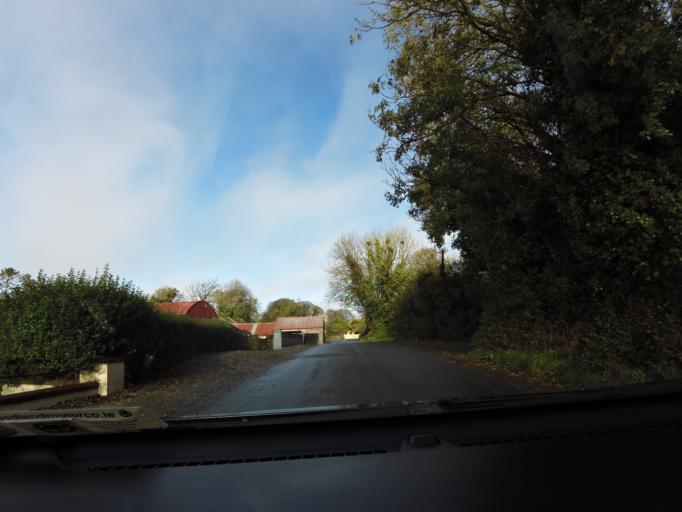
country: IE
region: Leinster
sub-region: An Iarmhi
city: Moate
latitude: 53.3910
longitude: -7.8090
